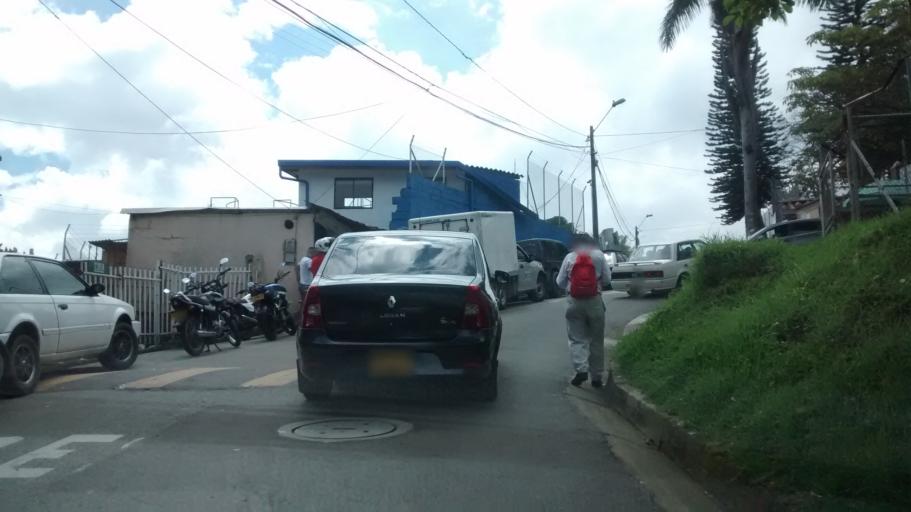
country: CO
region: Antioquia
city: La Estrella
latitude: 6.1791
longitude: -75.6615
